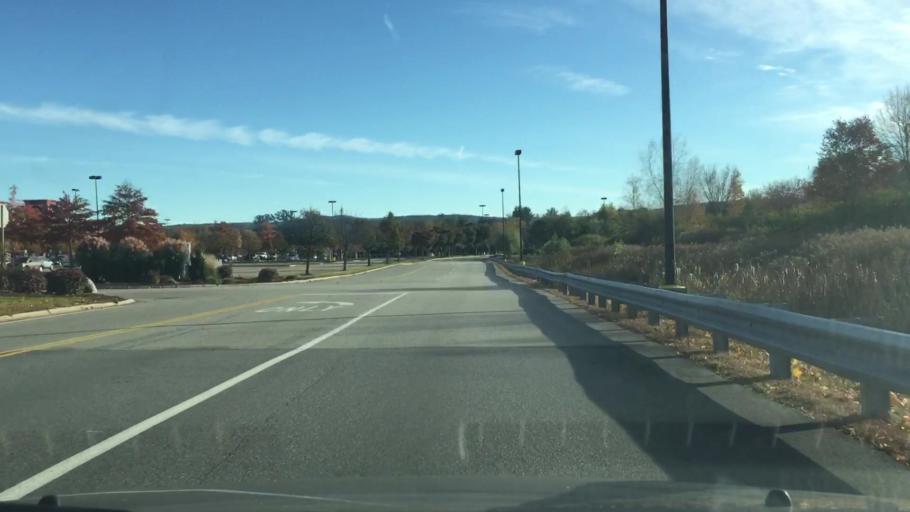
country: US
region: New Hampshire
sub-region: Cheshire County
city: Keene
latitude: 42.9266
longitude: -72.3044
